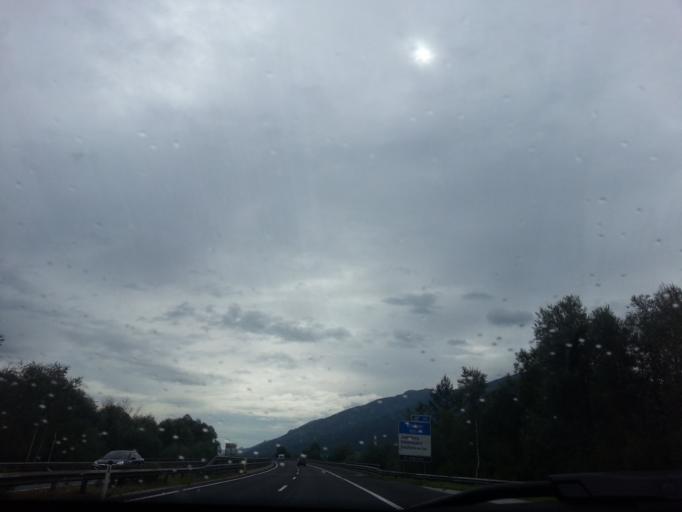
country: AT
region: Styria
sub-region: Politischer Bezirk Liezen
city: Trieben
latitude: 47.4981
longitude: 14.4669
